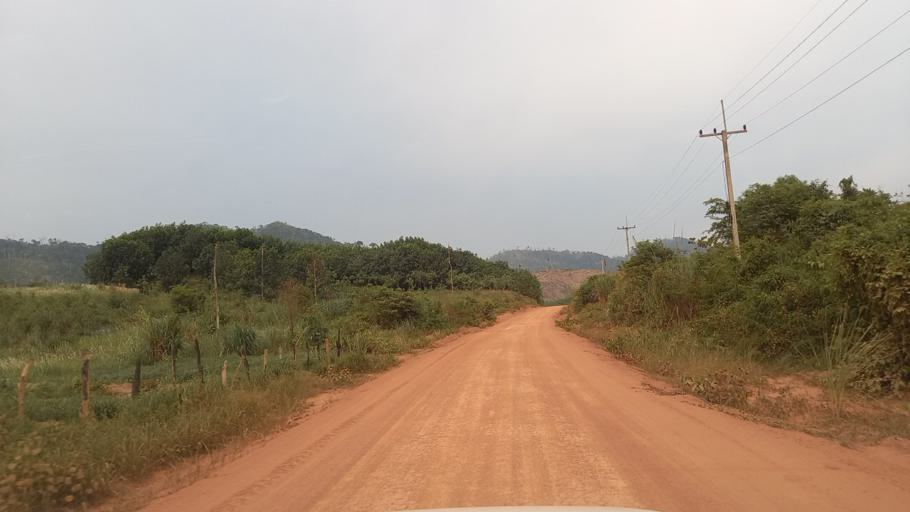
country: LA
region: Bolikhamxai
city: Bolikhan
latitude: 18.5359
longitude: 103.8128
